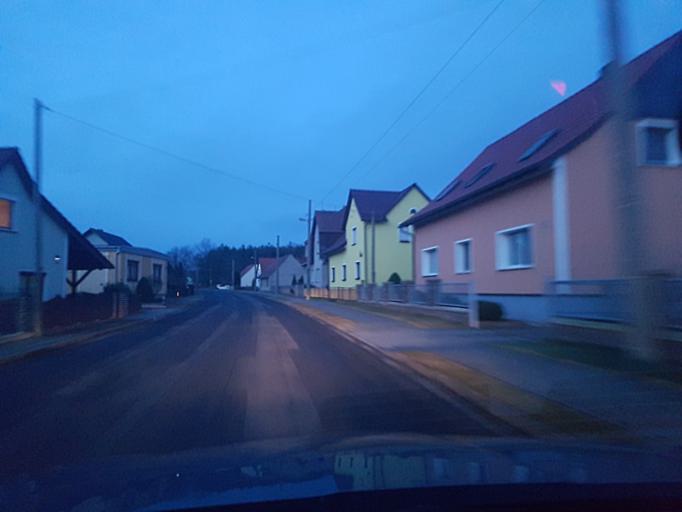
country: DE
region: Brandenburg
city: Bad Liebenwerda
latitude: 51.5482
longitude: 13.4238
